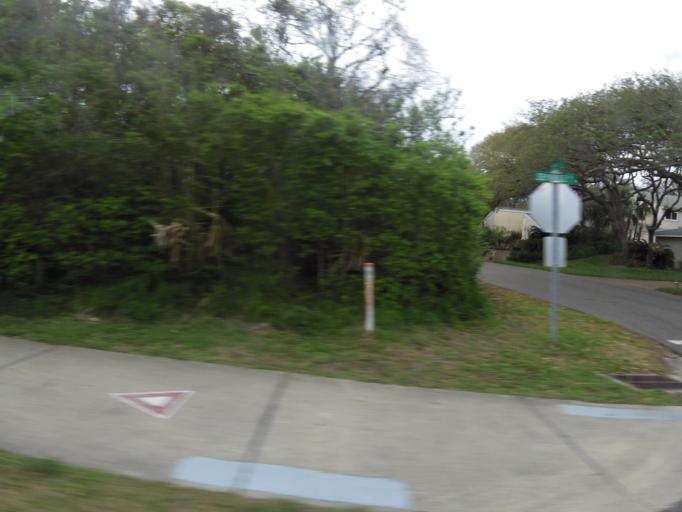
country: US
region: Florida
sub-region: Duval County
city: Atlantic Beach
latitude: 30.3527
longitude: -81.3996
